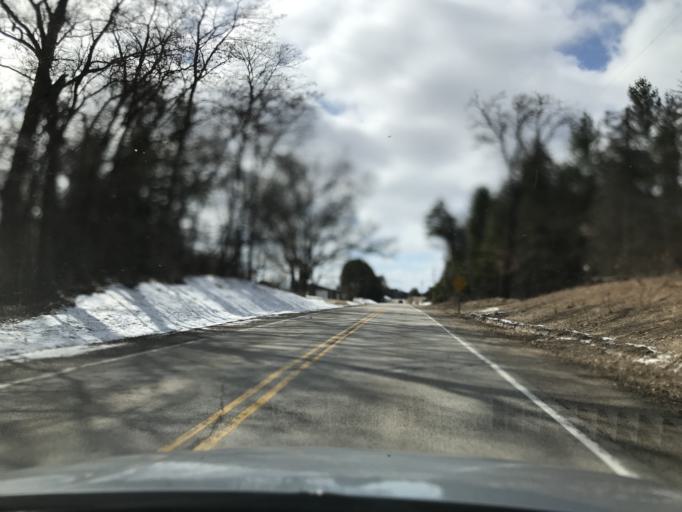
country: US
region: Wisconsin
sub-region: Marinette County
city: Peshtigo
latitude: 45.2466
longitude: -88.0479
